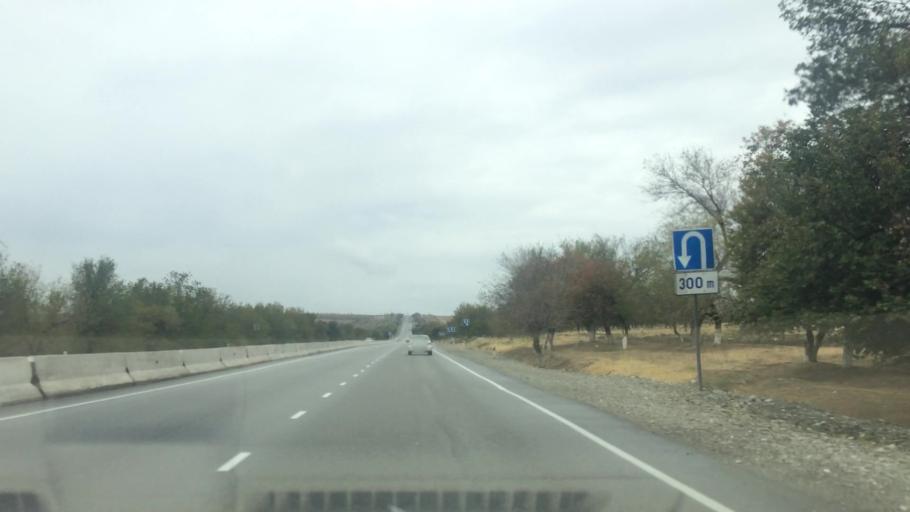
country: UZ
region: Samarqand
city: Bulung'ur
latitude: 39.8792
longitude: 67.4845
